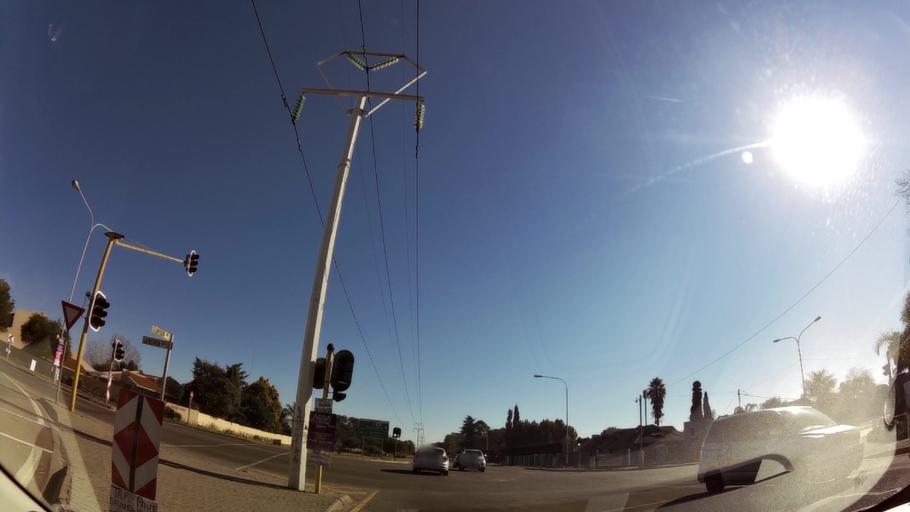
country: ZA
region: Gauteng
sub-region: City of Tshwane Metropolitan Municipality
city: Centurion
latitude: -25.8442
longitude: 28.2032
